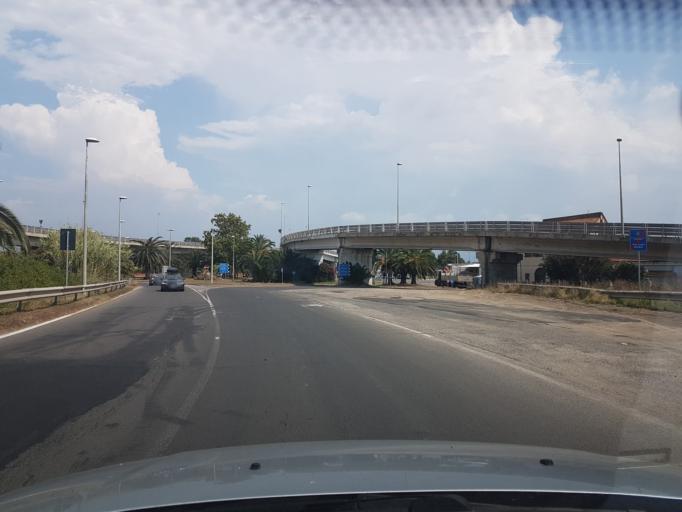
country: IT
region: Sardinia
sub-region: Provincia di Oristano
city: Donigala Fenugheddu
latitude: 39.9273
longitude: 8.5774
